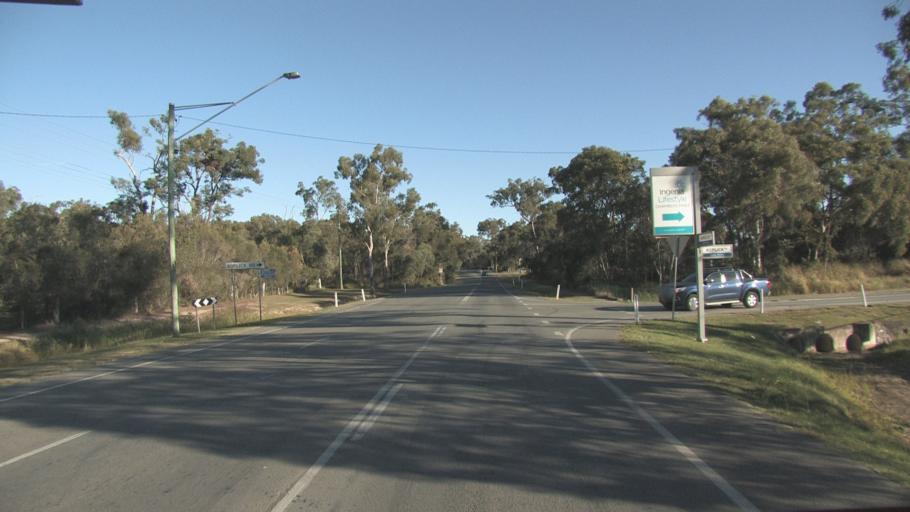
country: AU
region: Queensland
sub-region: Logan
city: Logan Reserve
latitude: -27.7207
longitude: 153.0909
